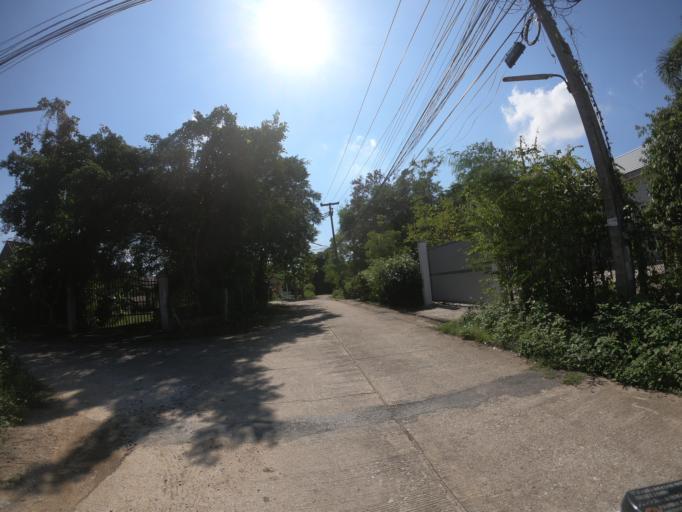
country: TH
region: Chiang Mai
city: Chiang Mai
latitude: 18.7469
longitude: 98.9694
